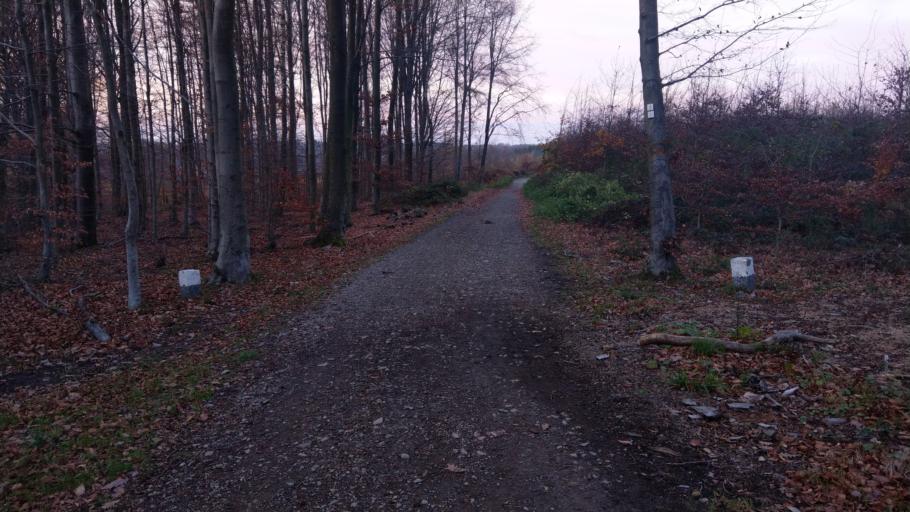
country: NL
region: Limburg
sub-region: Gemeente Vaals
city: Vaals
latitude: 50.7449
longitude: 6.0229
